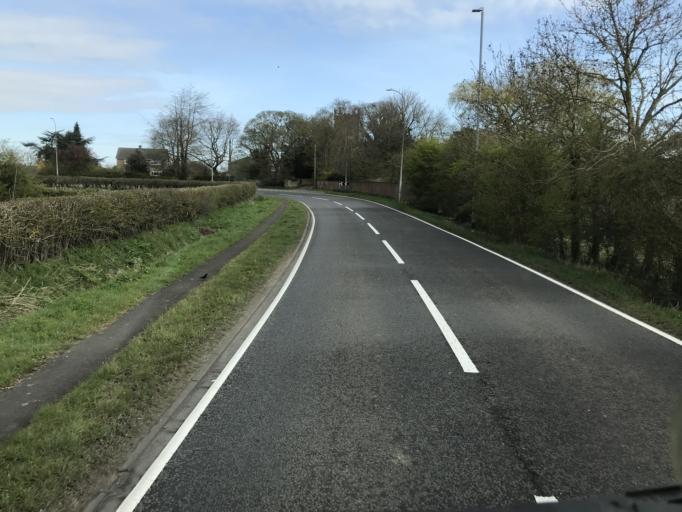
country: GB
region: England
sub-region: Lincolnshire
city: Market Rasen
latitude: 53.3885
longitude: -0.4006
